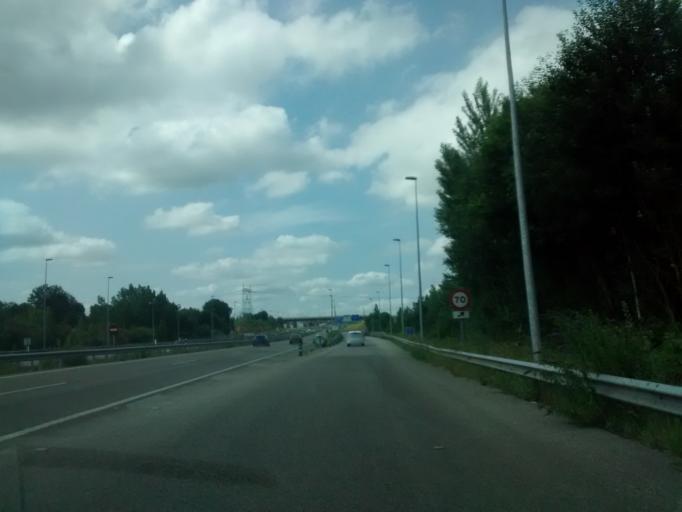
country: ES
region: Asturias
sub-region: Province of Asturias
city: Pola de Siero
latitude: 43.3771
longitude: -5.6848
